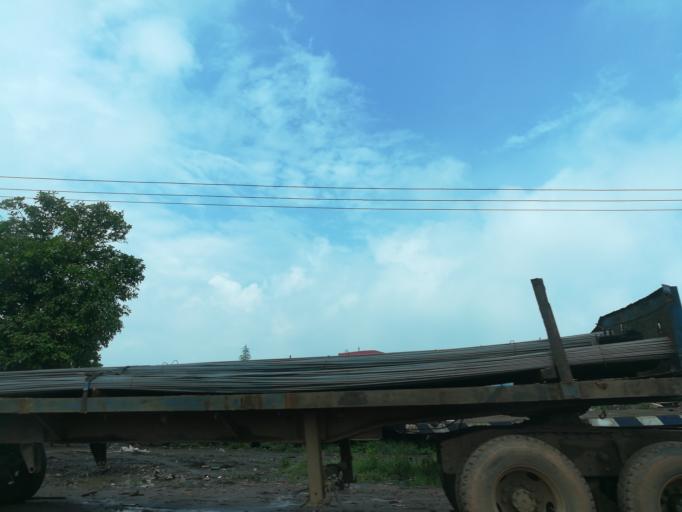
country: NG
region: Lagos
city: Ikorodu
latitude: 6.6684
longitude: 3.5139
